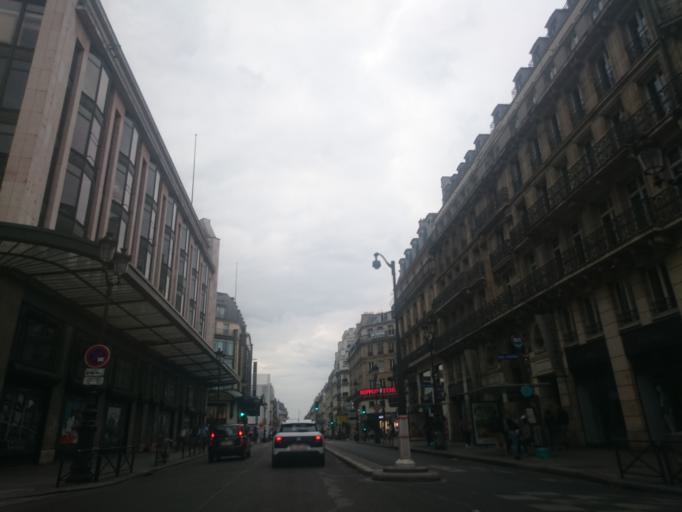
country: FR
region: Ile-de-France
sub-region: Paris
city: Paris
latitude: 48.8596
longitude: 2.3448
